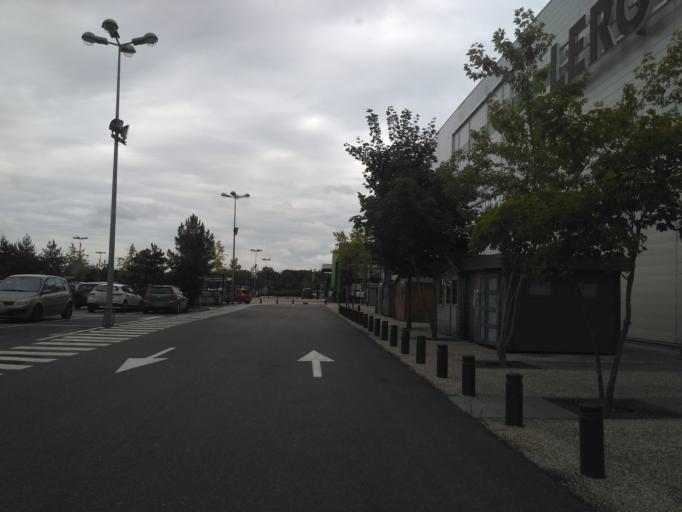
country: FR
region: Ile-de-France
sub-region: Departement de Seine-et-Marne
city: Vert-Saint-Denis
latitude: 48.5806
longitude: 2.6063
